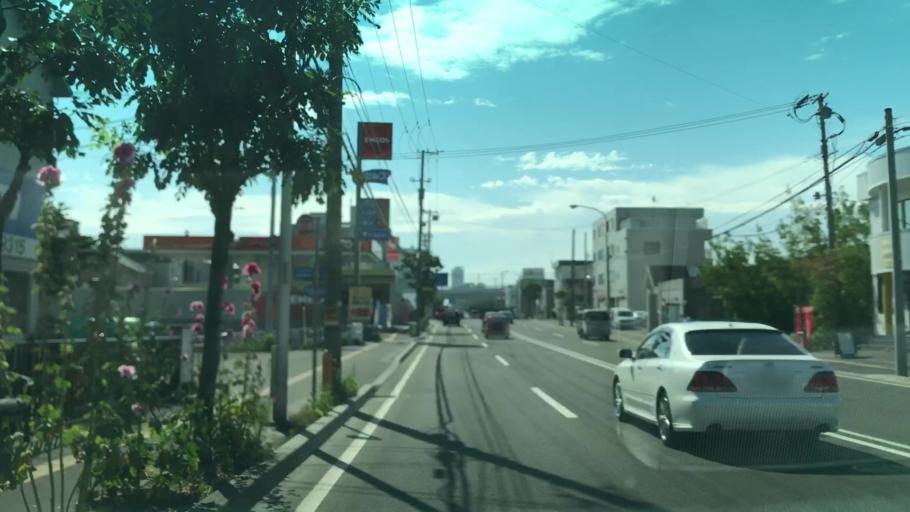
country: JP
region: Hokkaido
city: Sapporo
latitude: 43.0953
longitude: 141.2808
